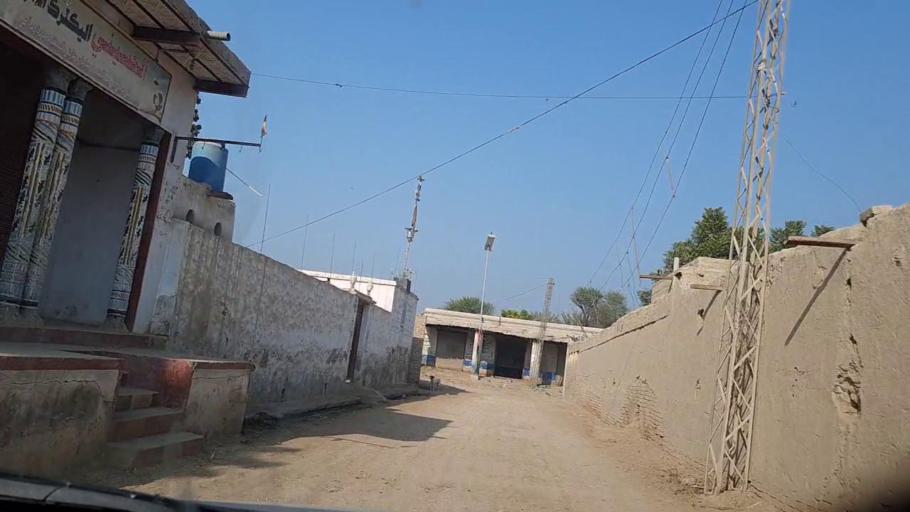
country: PK
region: Sindh
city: Moro
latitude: 26.7928
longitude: 67.9428
